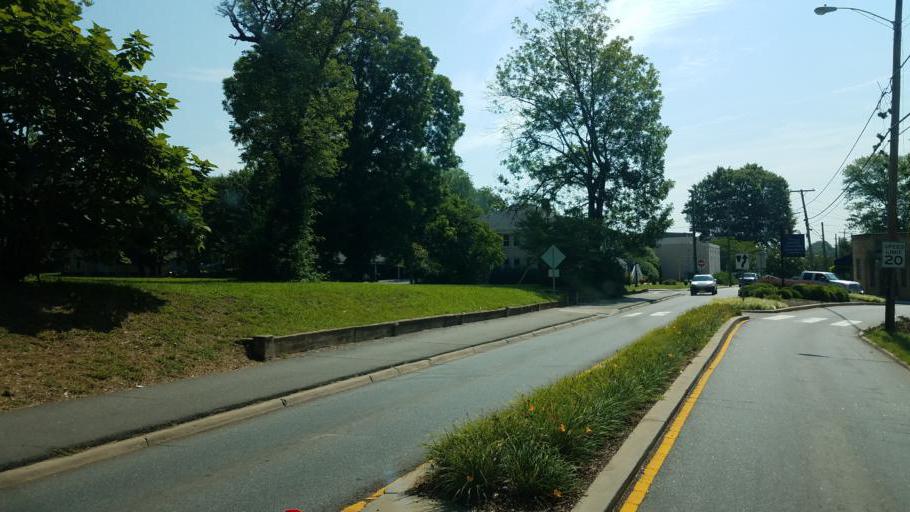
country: US
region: North Carolina
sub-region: Burke County
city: Morganton
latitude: 35.7479
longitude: -81.6918
